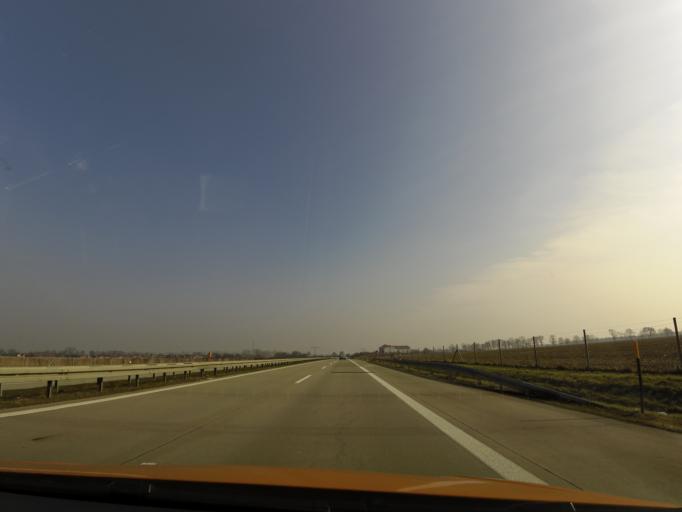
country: DE
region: Brandenburg
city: Mullrose
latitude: 52.3205
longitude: 14.4438
